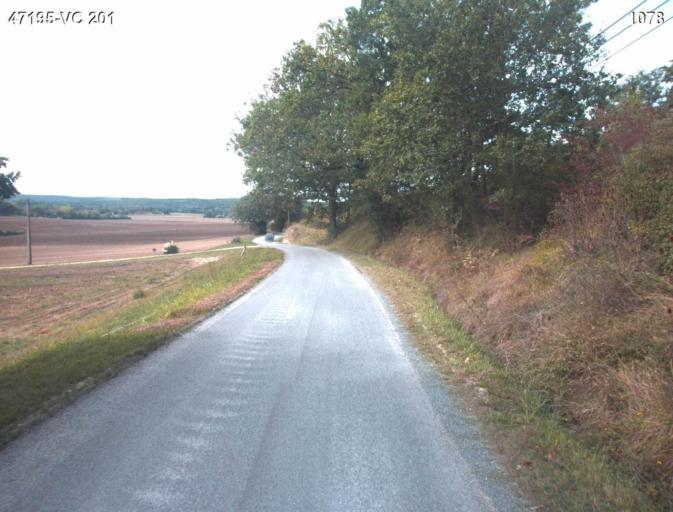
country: FR
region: Aquitaine
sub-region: Departement du Lot-et-Garonne
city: Barbaste
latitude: 44.1297
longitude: 0.3045
